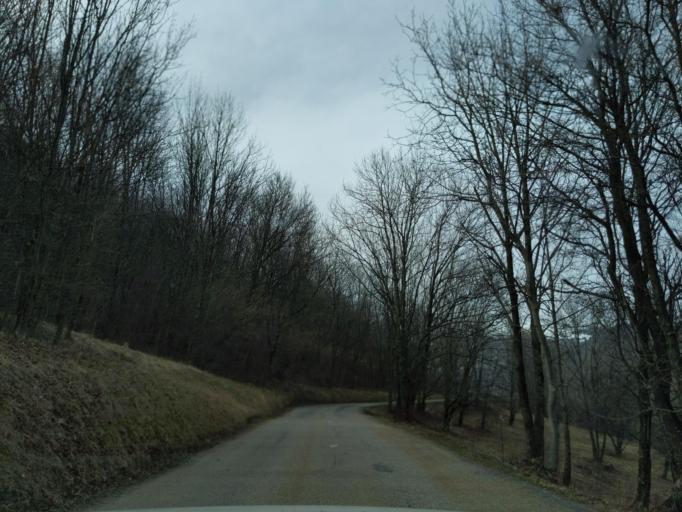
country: FR
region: Rhone-Alpes
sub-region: Departement de la Savoie
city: Villargondran
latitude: 45.2611
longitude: 6.3673
